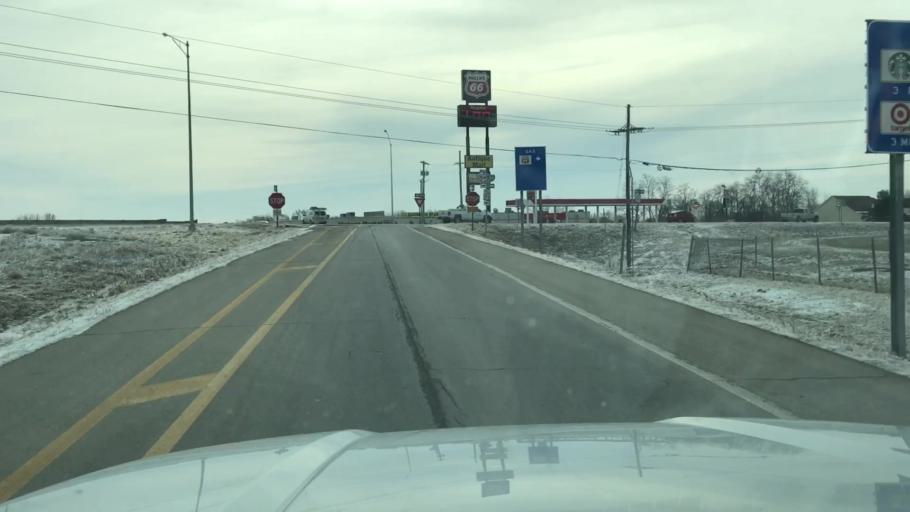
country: US
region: Missouri
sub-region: Andrew County
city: Country Club Village
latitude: 39.8579
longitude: -94.8118
